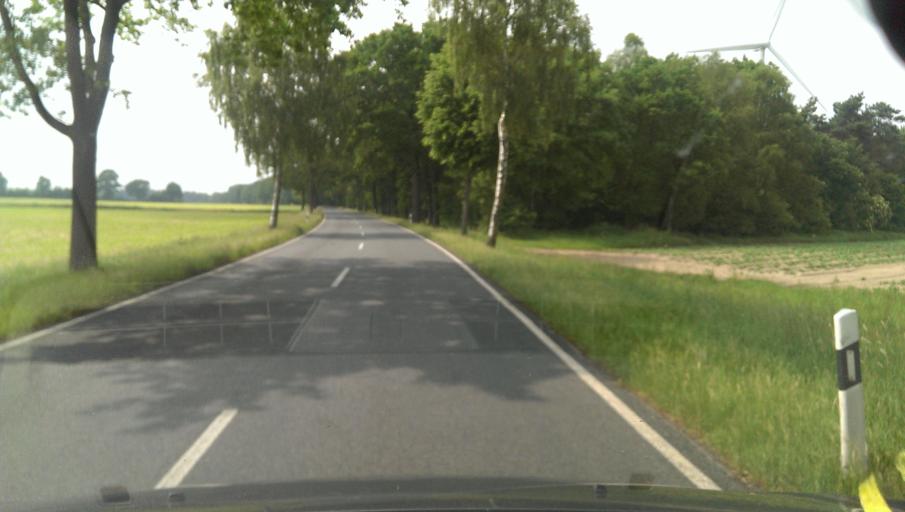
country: DE
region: Lower Saxony
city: Hankensbuttel
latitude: 52.7450
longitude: 10.5604
